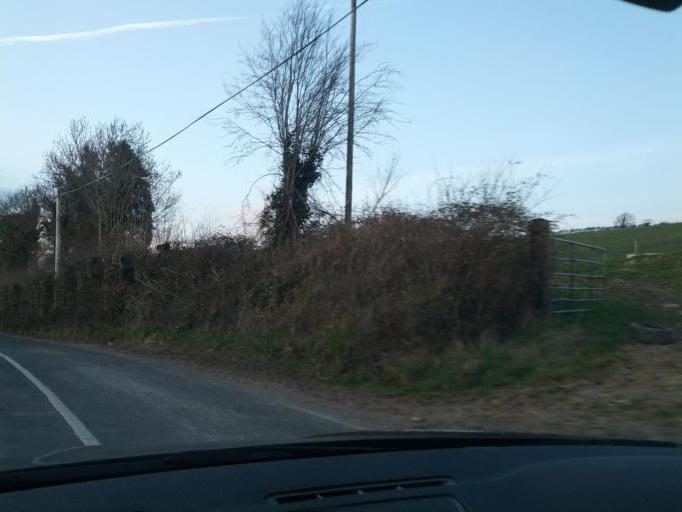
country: IE
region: Munster
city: Nenagh Bridge
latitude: 52.9169
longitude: -8.2168
